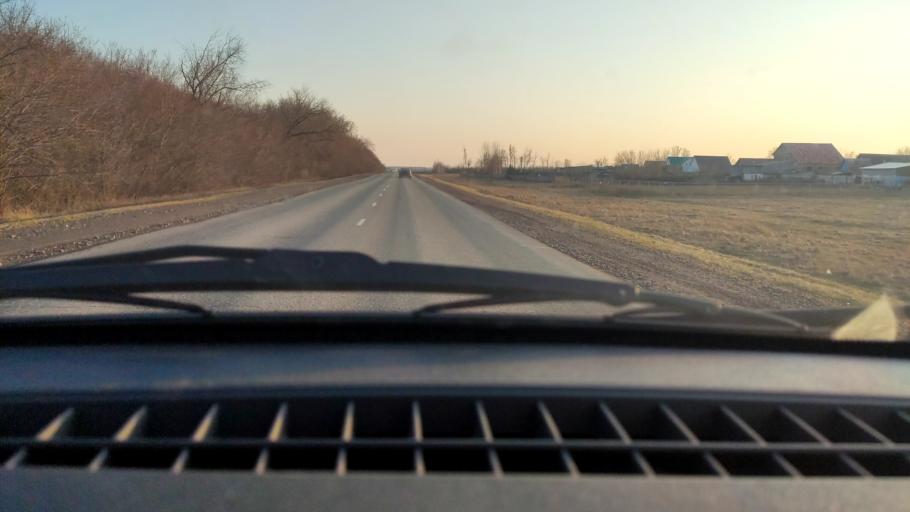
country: RU
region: Bashkortostan
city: Davlekanovo
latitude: 54.2921
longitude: 55.1222
